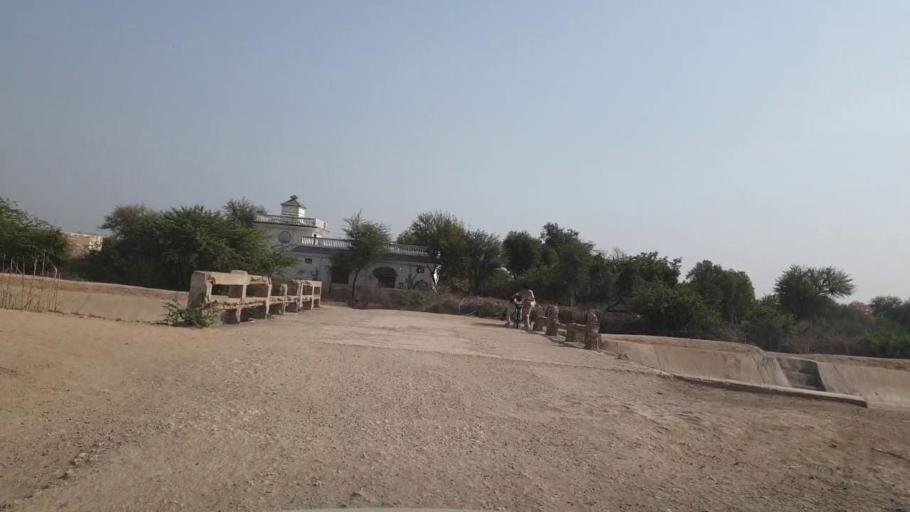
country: PK
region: Sindh
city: Dhoro Naro
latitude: 25.4817
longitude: 69.6561
